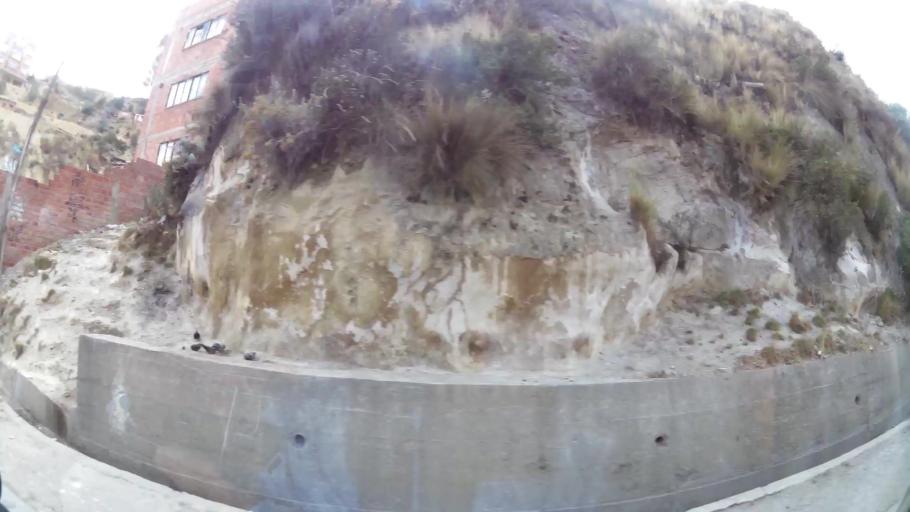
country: BO
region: La Paz
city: La Paz
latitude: -16.4682
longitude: -68.1196
